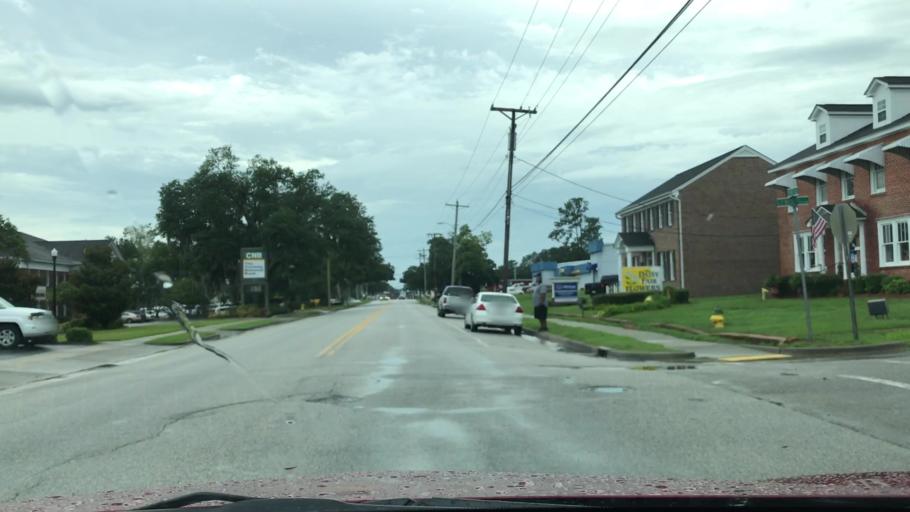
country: US
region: South Carolina
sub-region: Horry County
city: Conway
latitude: 33.8339
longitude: -79.0521
